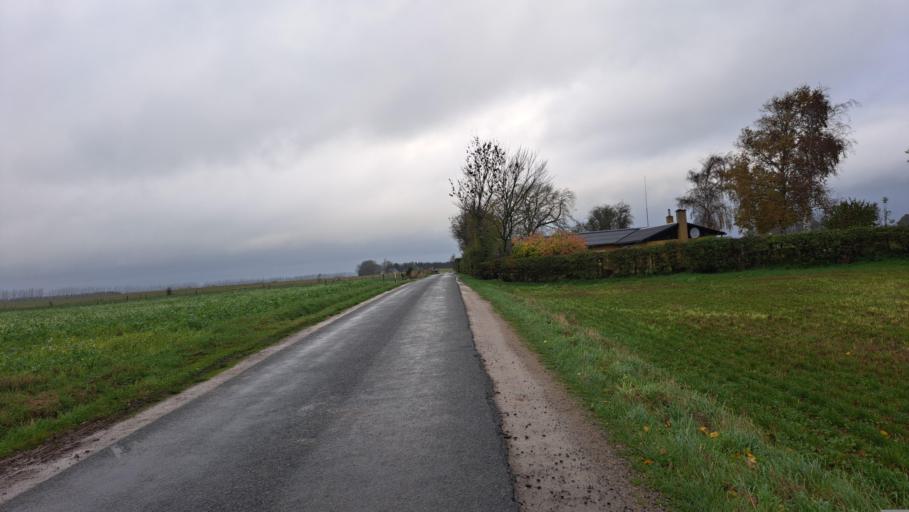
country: DK
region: Central Jutland
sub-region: Hedensted Kommune
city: Hedensted
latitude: 55.8287
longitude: 9.7318
